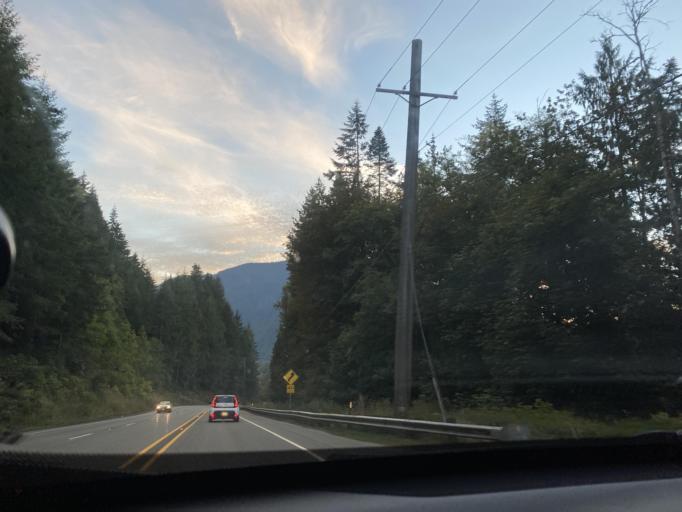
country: US
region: Washington
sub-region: Clallam County
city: Port Angeles
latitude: 48.0719
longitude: -123.5709
